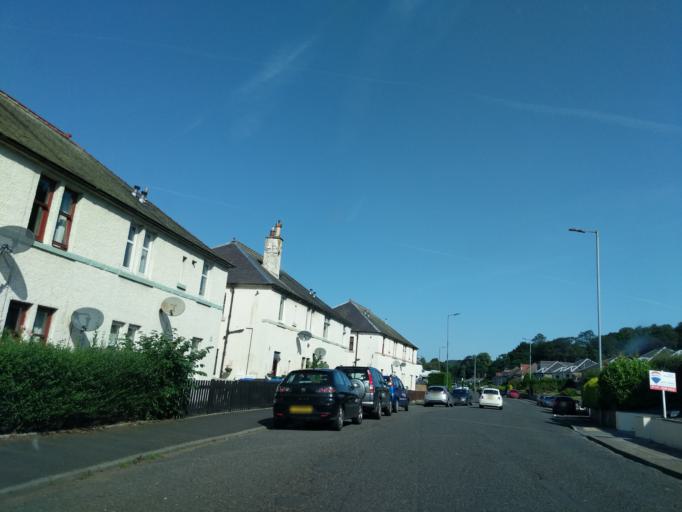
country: GB
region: Scotland
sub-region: The Scottish Borders
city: Peebles
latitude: 55.6600
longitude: -3.1922
